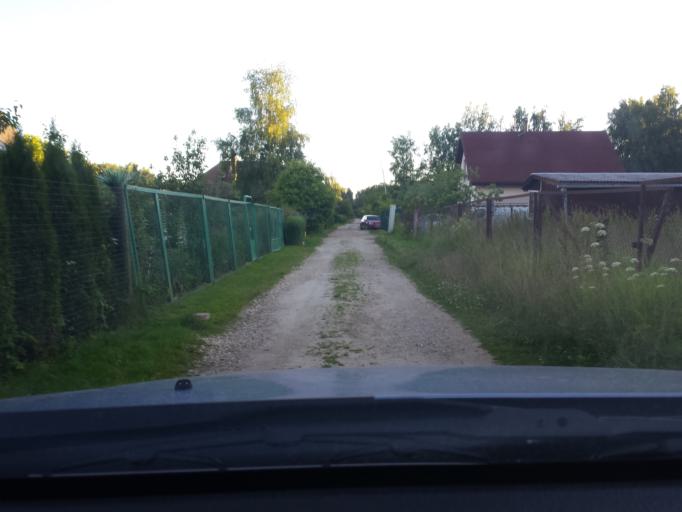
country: LV
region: Carnikava
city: Carnikava
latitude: 57.1263
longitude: 24.2385
